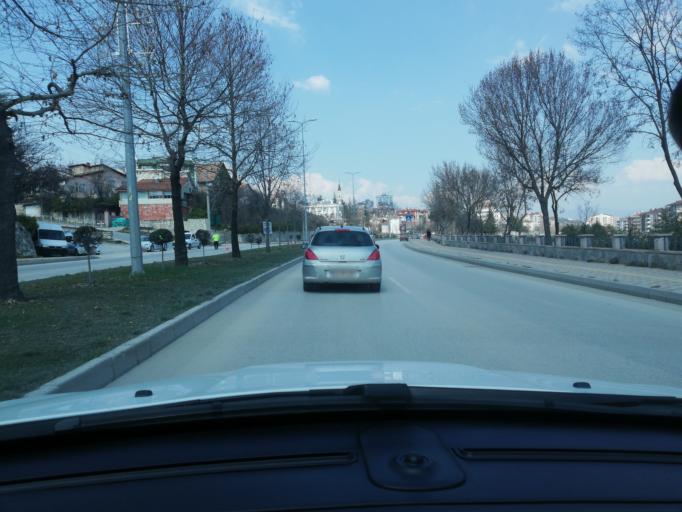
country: TR
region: Kastamonu
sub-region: Cide
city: Kastamonu
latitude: 41.3990
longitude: 33.7807
